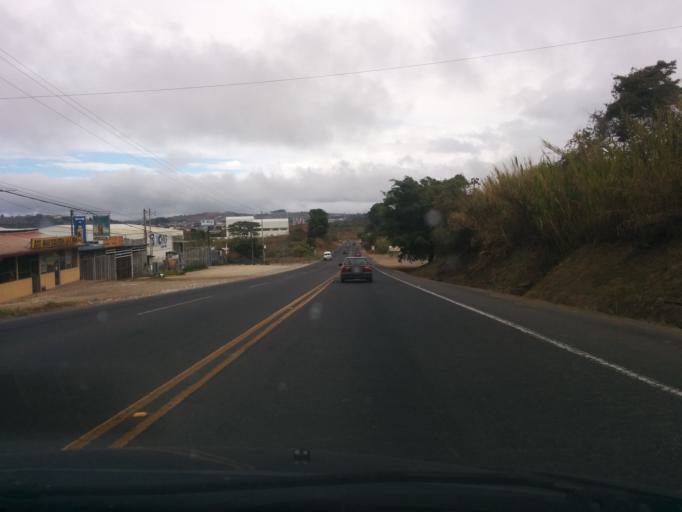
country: CR
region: Alajuela
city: San Rafael
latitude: 10.0666
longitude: -84.4533
